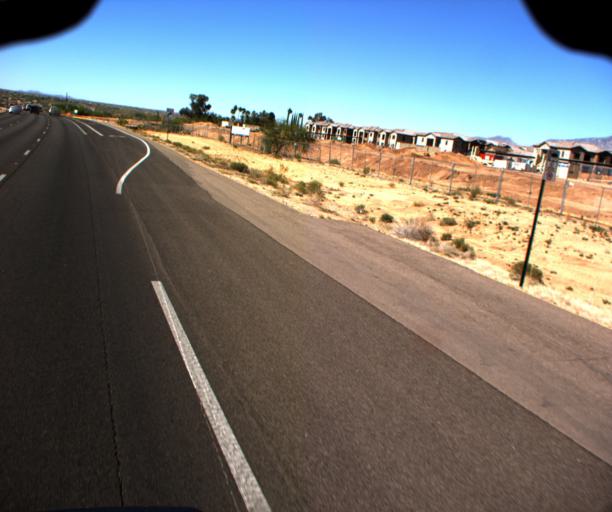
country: US
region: Arizona
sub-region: Pima County
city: Oro Valley
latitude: 32.3813
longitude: -110.9638
